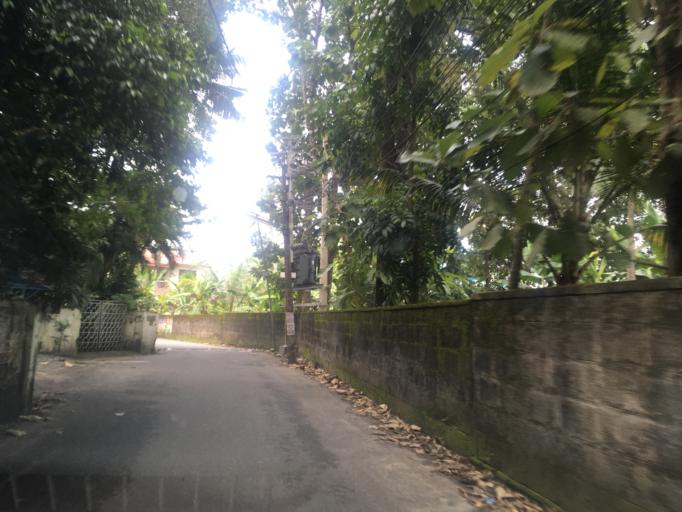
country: IN
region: Kerala
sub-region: Ernakulam
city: Elur
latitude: 10.0338
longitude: 76.3074
